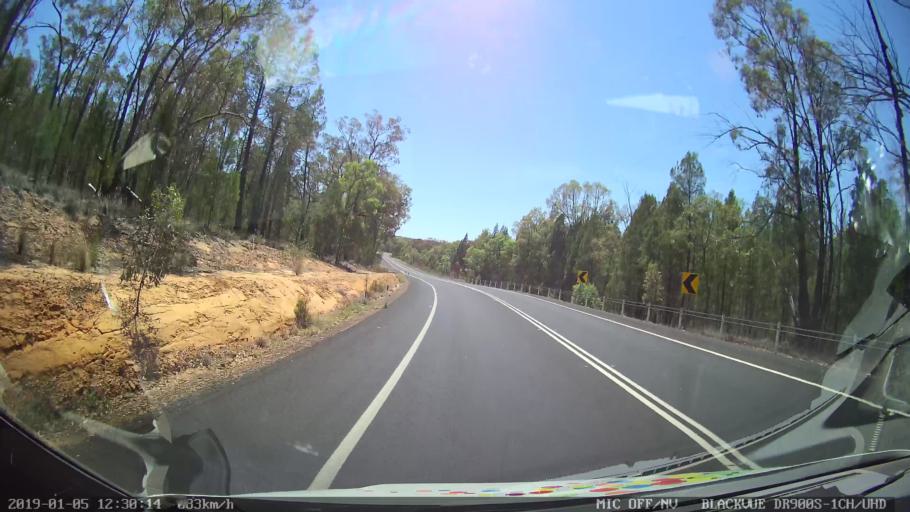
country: AU
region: New South Wales
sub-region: Warrumbungle Shire
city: Coonabarabran
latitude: -31.2293
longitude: 149.3480
